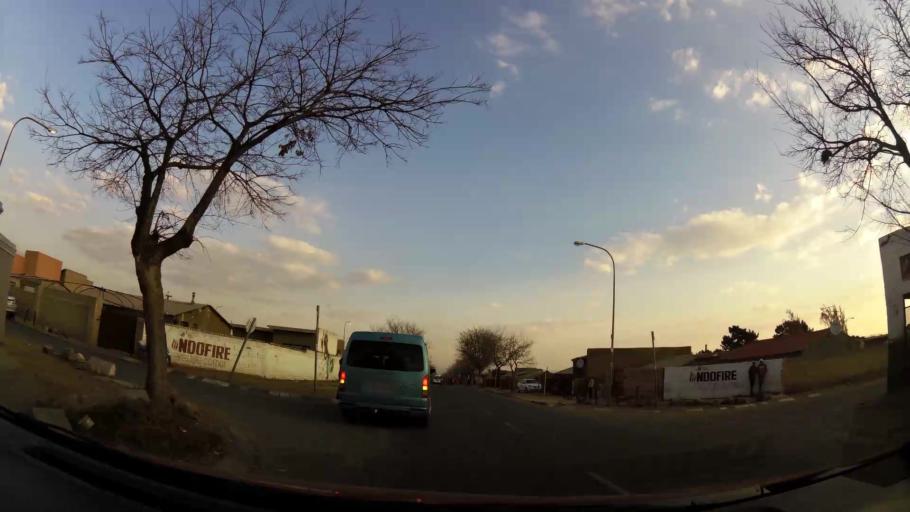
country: ZA
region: Gauteng
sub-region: City of Johannesburg Metropolitan Municipality
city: Roodepoort
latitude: -26.2162
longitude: 27.8934
